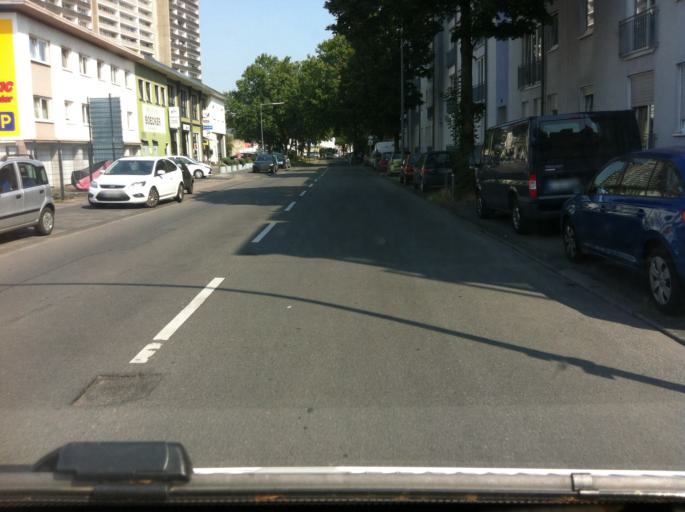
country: DE
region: North Rhine-Westphalia
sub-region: Regierungsbezirk Koln
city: Bilderstoeckchen
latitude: 50.9554
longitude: 6.8998
